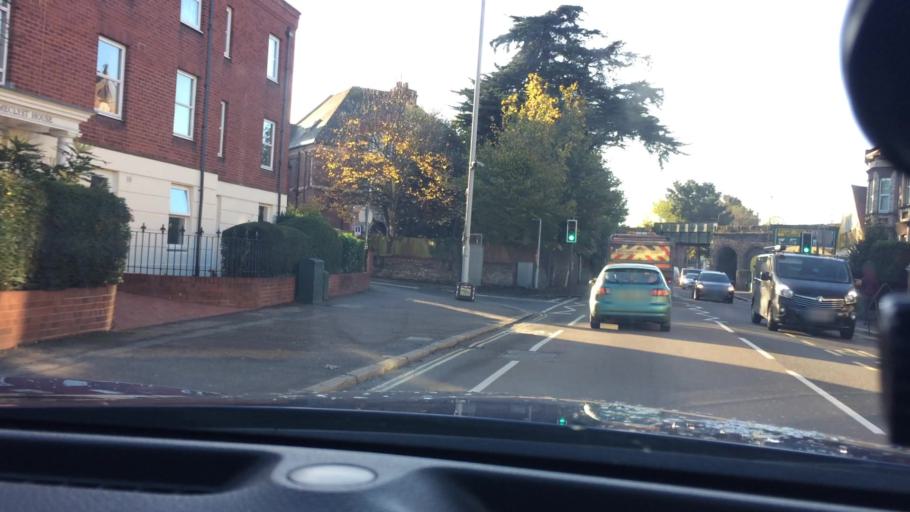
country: GB
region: England
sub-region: Devon
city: Exeter
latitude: 50.7158
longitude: -3.5359
